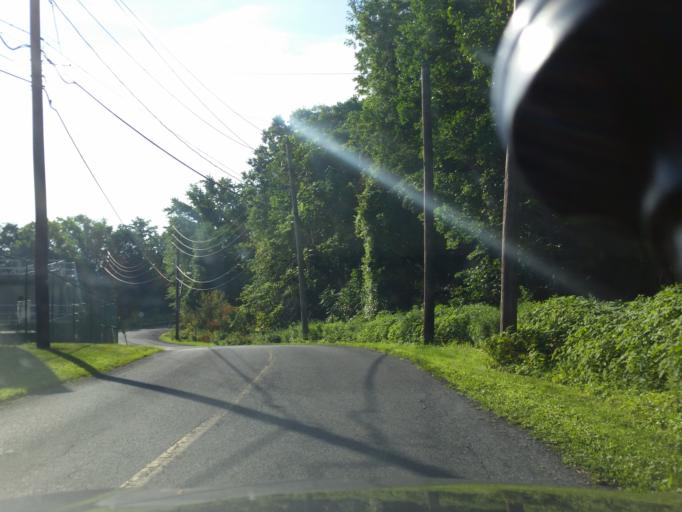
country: US
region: Pennsylvania
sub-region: Perry County
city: Marysville
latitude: 40.3323
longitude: -76.9191
